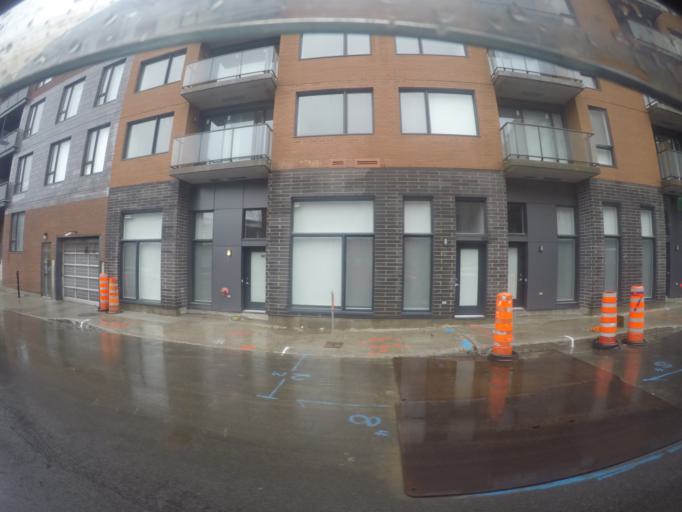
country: CA
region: Quebec
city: Montreal-Ouest
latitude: 45.4135
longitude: -73.6563
